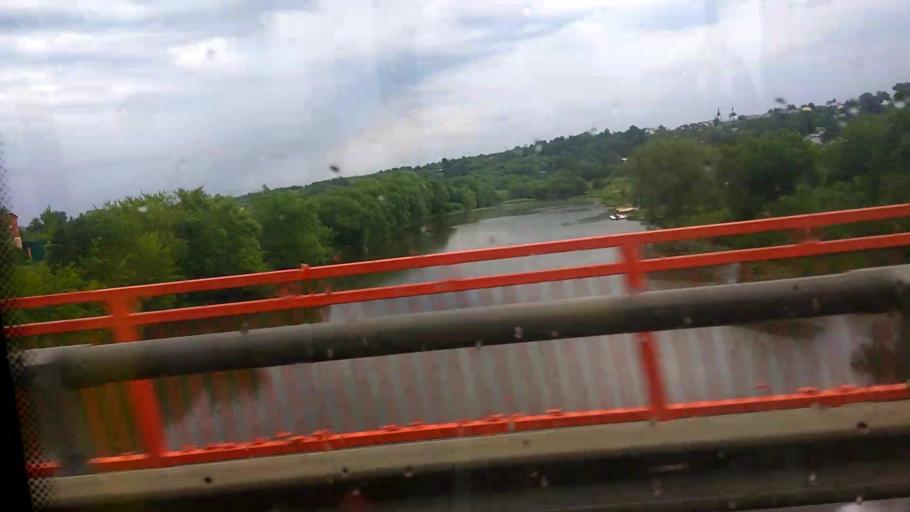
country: RU
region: Moskovskaya
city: Zaraysk
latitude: 54.7562
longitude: 38.8602
